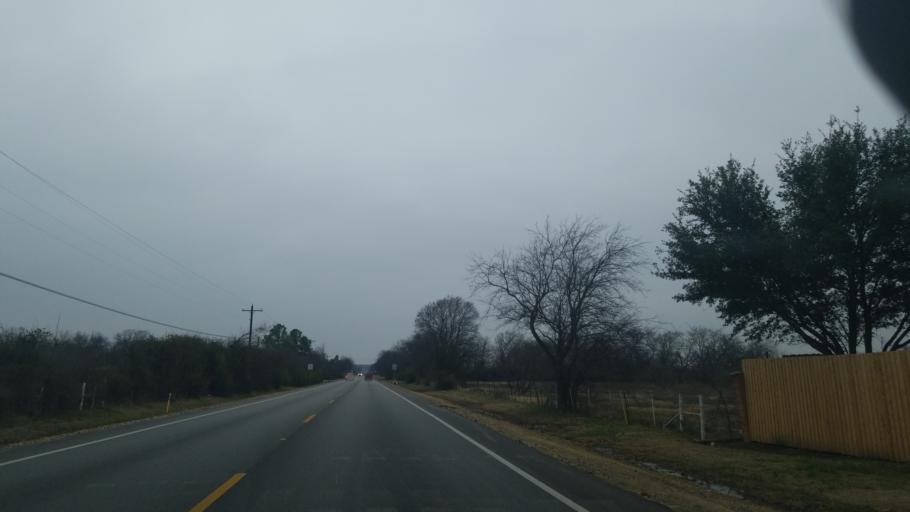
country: US
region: Texas
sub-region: Denton County
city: Denton
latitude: 33.1671
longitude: -97.1419
